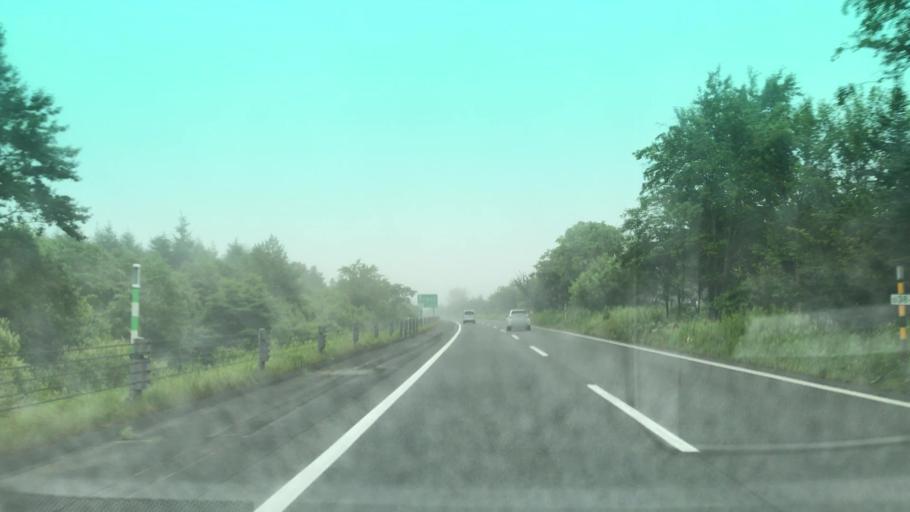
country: JP
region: Hokkaido
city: Chitose
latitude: 42.7849
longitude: 141.6264
